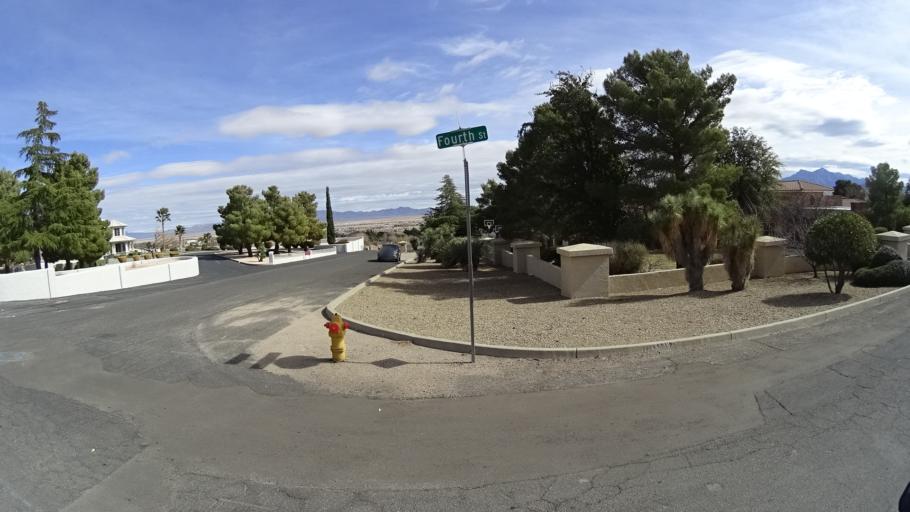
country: US
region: Arizona
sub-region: Mohave County
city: New Kingman-Butler
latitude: 35.2356
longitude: -114.0535
